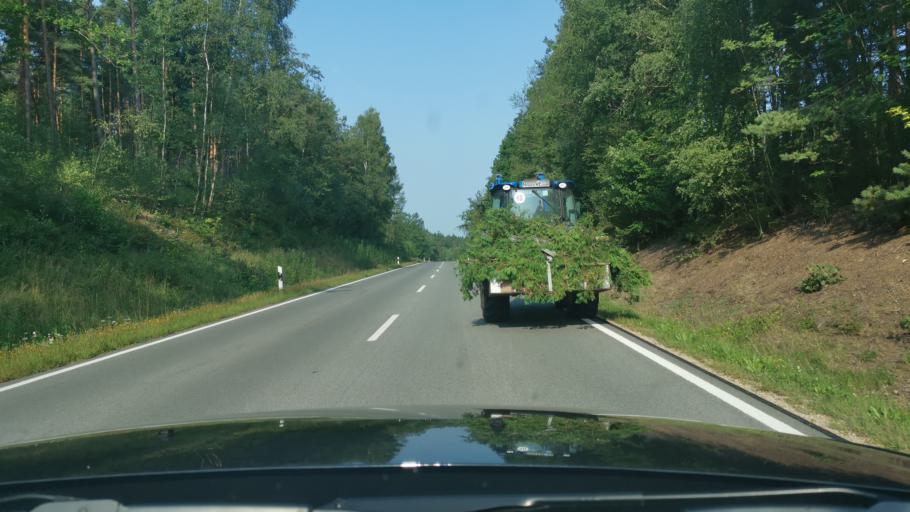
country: DE
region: Bavaria
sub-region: Upper Palatinate
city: Schnaittenbach
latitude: 49.5476
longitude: 12.0484
